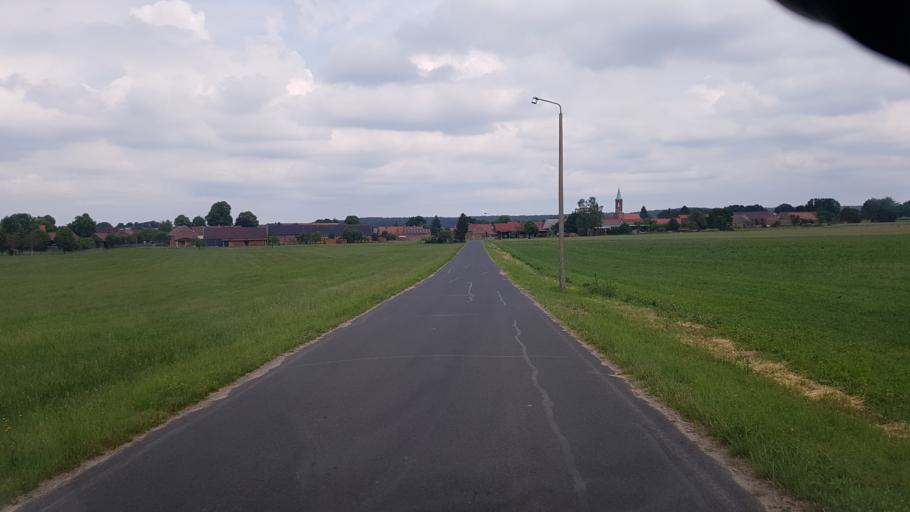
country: DE
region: Brandenburg
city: Lebusa
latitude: 51.8212
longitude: 13.4536
